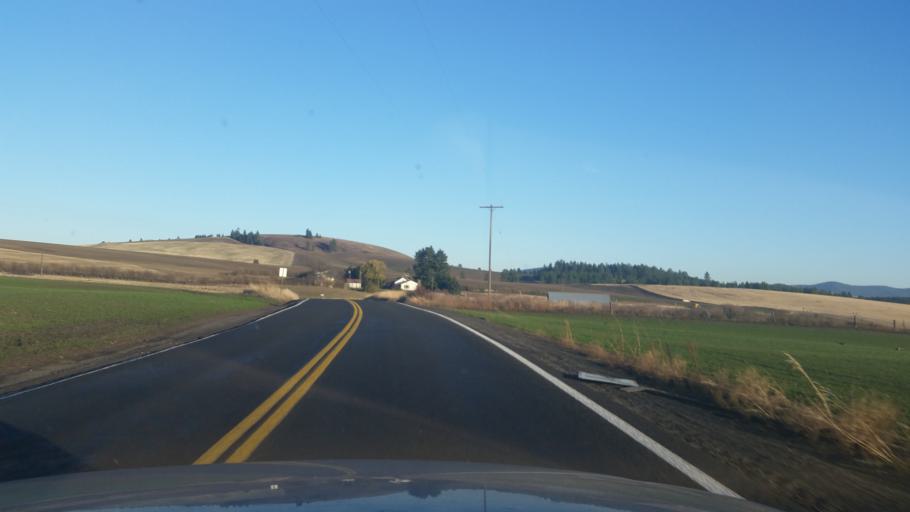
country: US
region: Washington
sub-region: Spokane County
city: Opportunity
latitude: 47.3504
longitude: -117.2342
